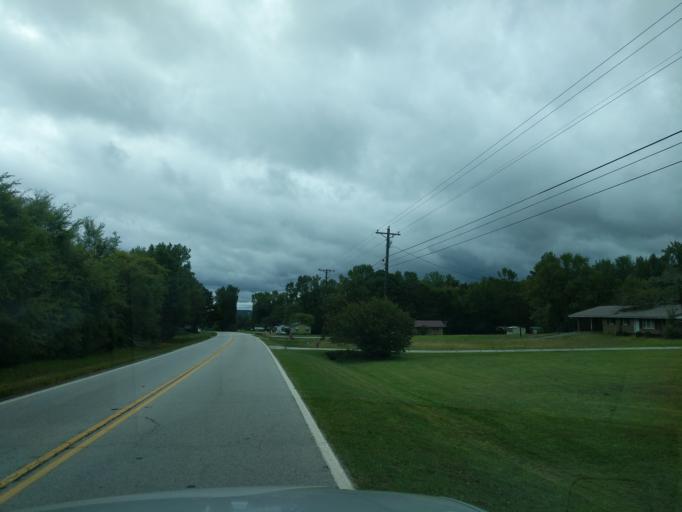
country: US
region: Georgia
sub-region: Elbert County
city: Elberton
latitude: 34.0594
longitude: -82.8291
